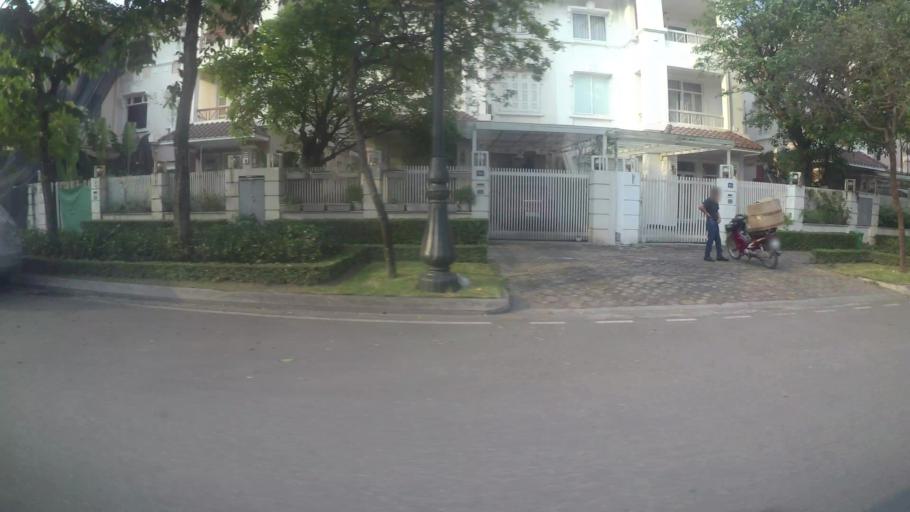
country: VN
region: Ha Noi
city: Tay Ho
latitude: 21.0769
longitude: 105.7956
